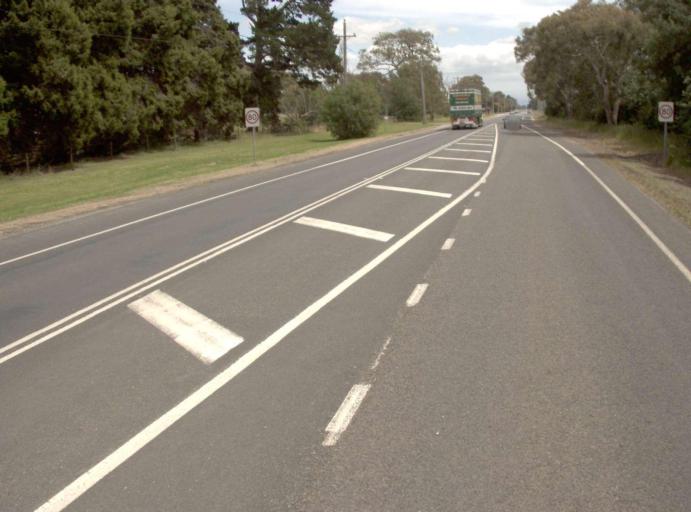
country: AU
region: Victoria
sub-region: Wellington
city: Sale
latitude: -38.0865
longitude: 147.0593
